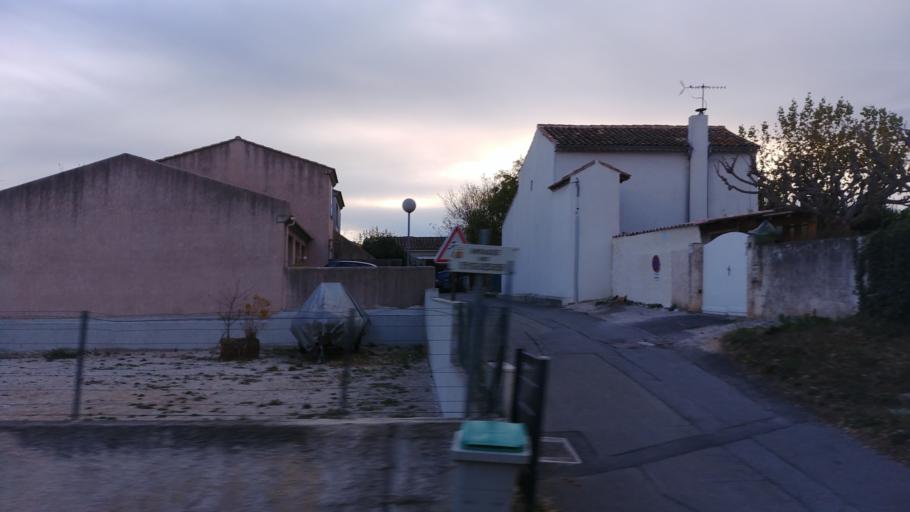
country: FR
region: Provence-Alpes-Cote d'Azur
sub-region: Departement des Bouches-du-Rhone
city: Venelles
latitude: 43.5798
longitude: 5.4708
